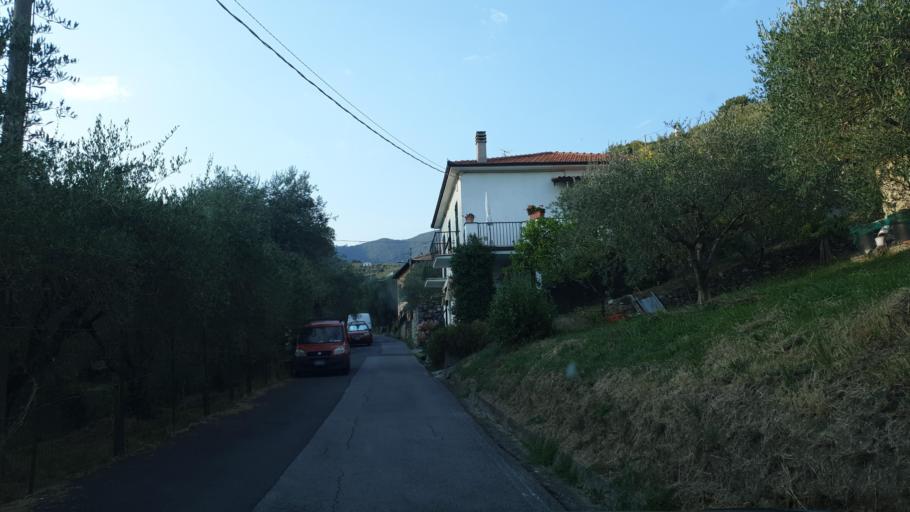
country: IT
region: Liguria
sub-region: Provincia di La Spezia
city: Levanto
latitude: 44.1788
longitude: 9.6191
